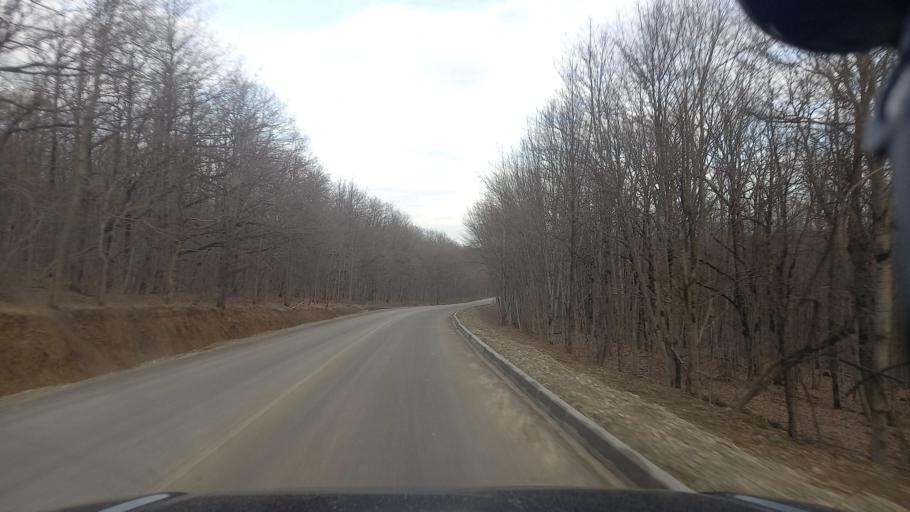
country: RU
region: Krasnodarskiy
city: Goryachiy Klyuch
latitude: 44.7089
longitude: 39.0077
